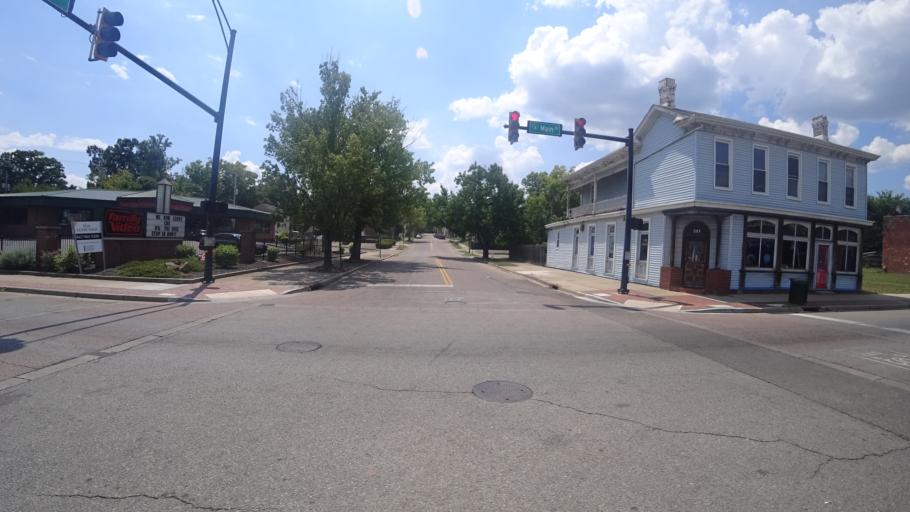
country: US
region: Ohio
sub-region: Butler County
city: Hamilton
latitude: 39.4055
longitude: -84.5716
